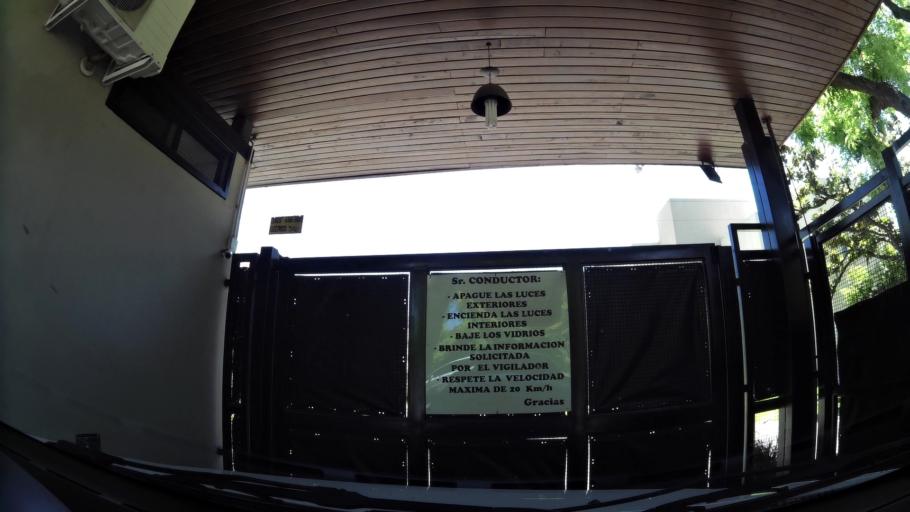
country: AR
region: Buenos Aires
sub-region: Partido de San Isidro
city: San Isidro
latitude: -34.4911
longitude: -58.5703
